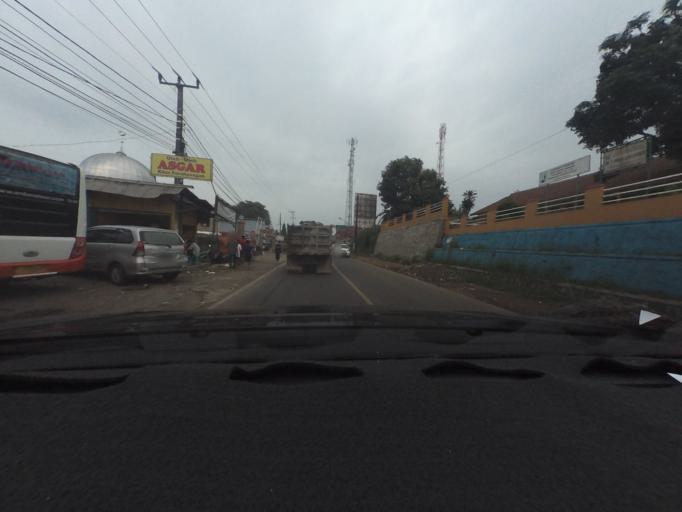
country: ID
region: West Java
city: Cicurug
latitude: -6.8142
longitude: 106.7678
